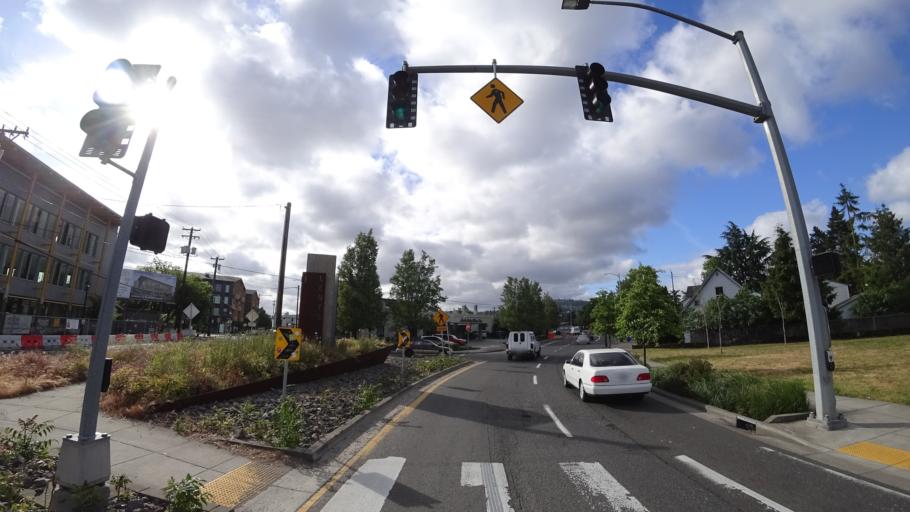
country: US
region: Oregon
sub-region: Multnomah County
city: Lents
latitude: 45.4804
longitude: -122.5708
